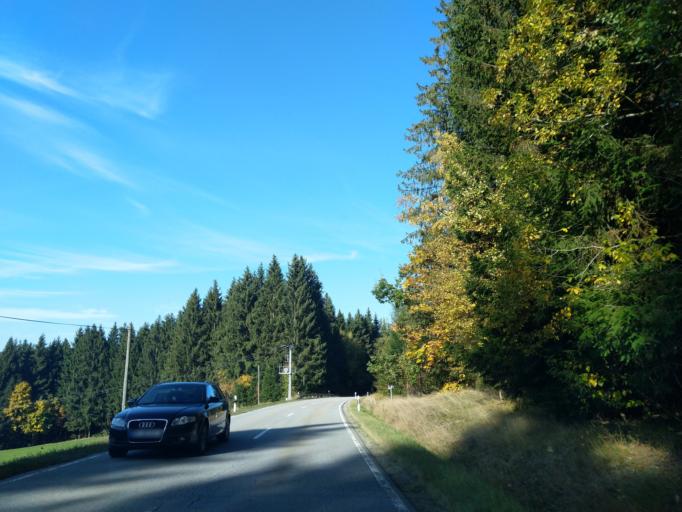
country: DE
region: Bavaria
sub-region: Lower Bavaria
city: Achslach
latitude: 48.9561
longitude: 12.9250
